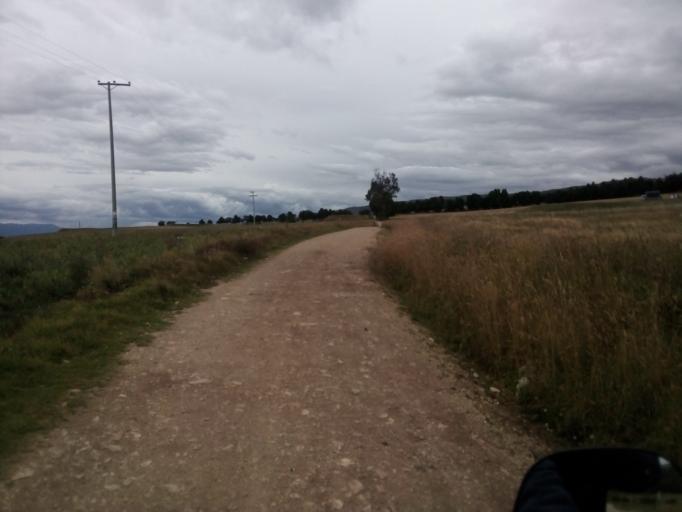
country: CO
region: Boyaca
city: Toca
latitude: 5.5898
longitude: -73.1372
